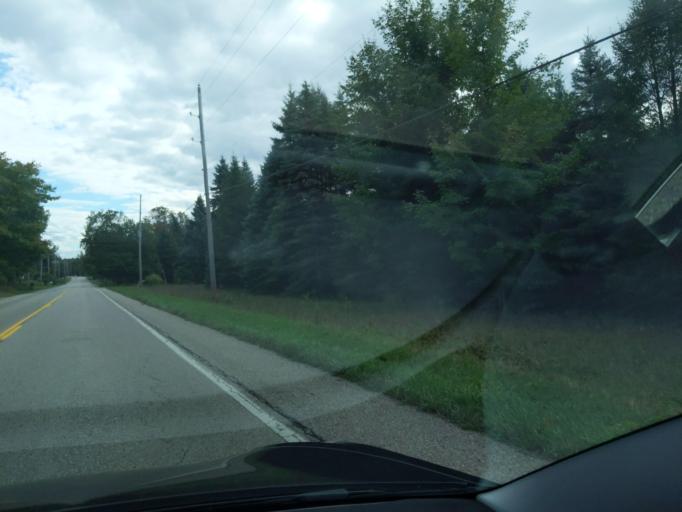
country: US
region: Michigan
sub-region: Kalkaska County
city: Rapid City
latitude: 44.9130
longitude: -85.2840
